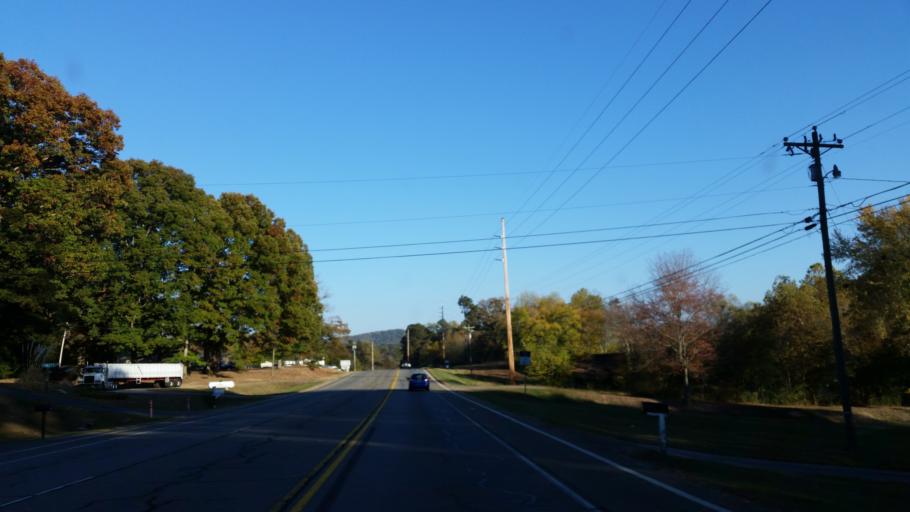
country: US
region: Georgia
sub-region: Gilmer County
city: Ellijay
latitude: 34.6515
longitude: -84.4069
